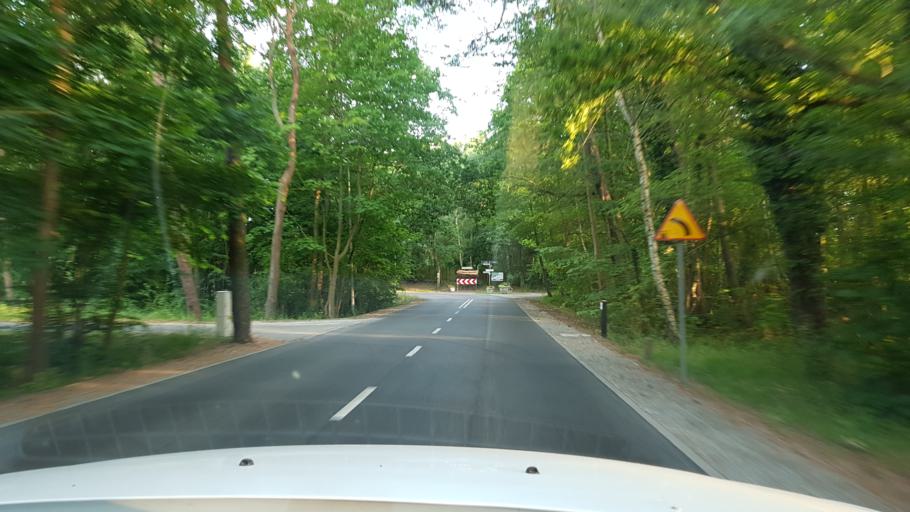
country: PL
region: West Pomeranian Voivodeship
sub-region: Swinoujscie
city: Swinoujscie
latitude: 53.8530
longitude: 14.2860
